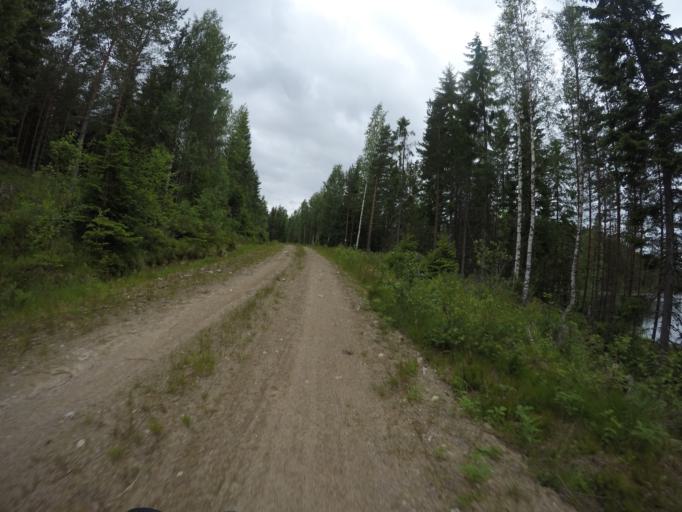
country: SE
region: Dalarna
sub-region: Ludvika Kommun
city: Abborrberget
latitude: 60.0661
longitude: 14.5617
